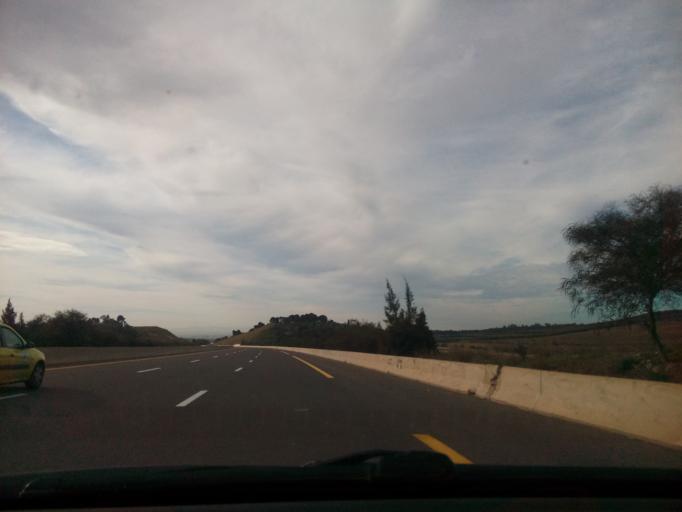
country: DZ
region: Sidi Bel Abbes
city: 'Ain el Berd
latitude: 35.3563
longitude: -0.5105
